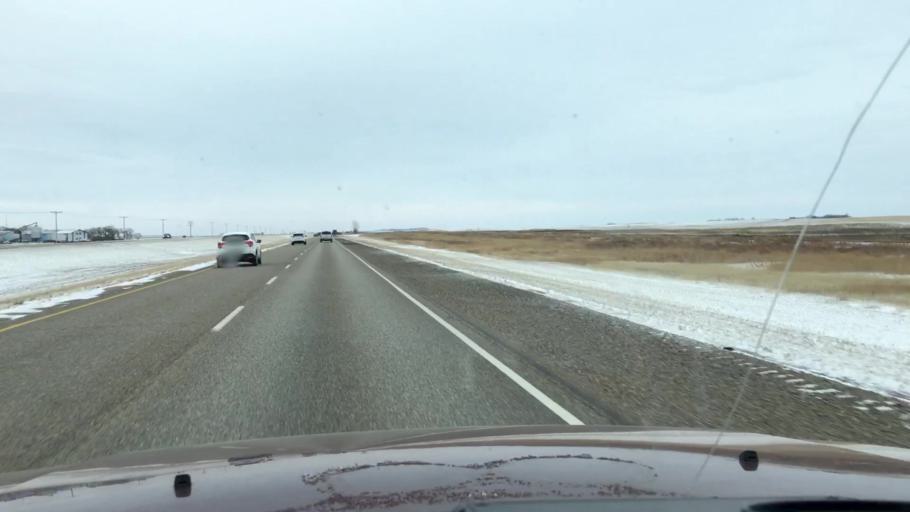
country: CA
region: Saskatchewan
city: Moose Jaw
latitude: 51.0127
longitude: -105.7778
